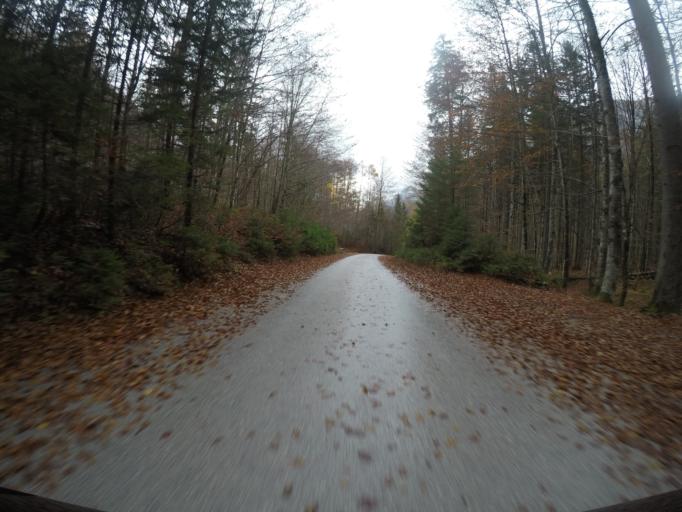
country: SI
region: Kranjska Gora
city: Mojstrana
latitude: 46.4165
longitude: 13.8518
